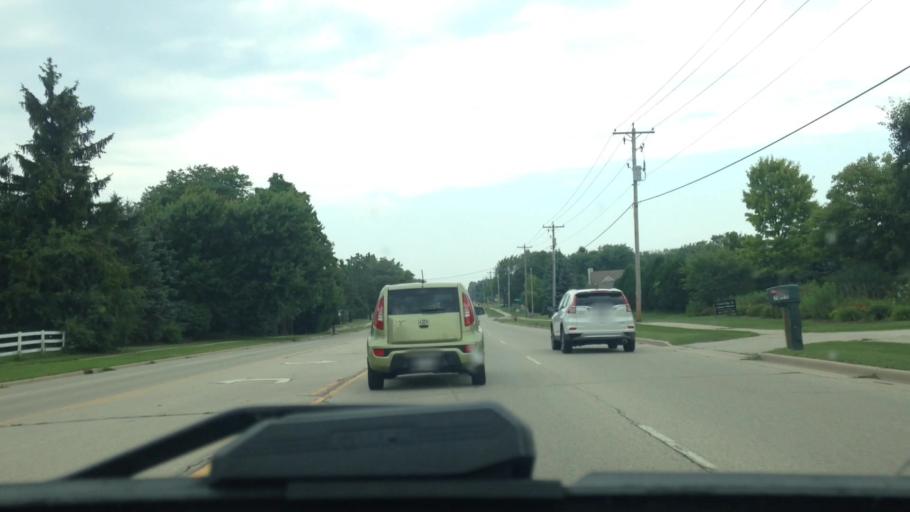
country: US
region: Wisconsin
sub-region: Waukesha County
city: Menomonee Falls
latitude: 43.1516
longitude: -88.1043
